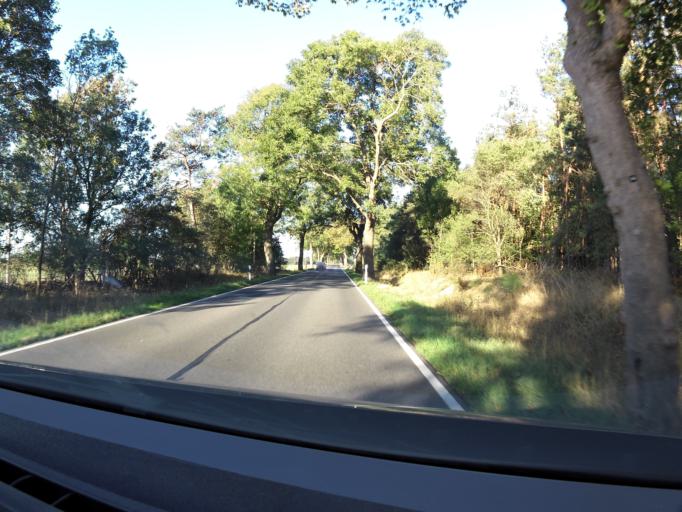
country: DE
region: Mecklenburg-Vorpommern
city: Alt-Sanitz
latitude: 53.8490
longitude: 13.6191
